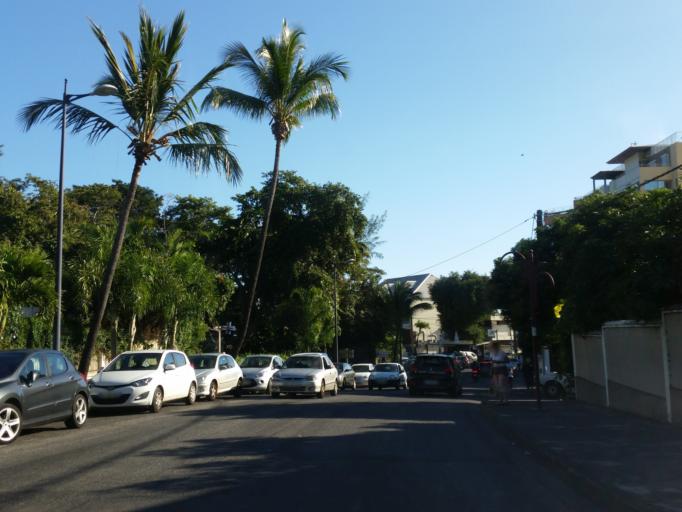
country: RE
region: Reunion
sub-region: Reunion
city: Saint-Denis
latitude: -20.8951
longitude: 55.4575
